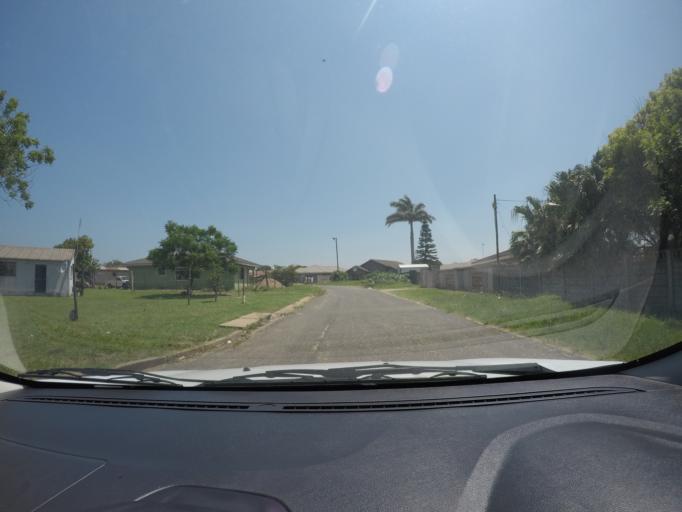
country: ZA
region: KwaZulu-Natal
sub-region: uThungulu District Municipality
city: eSikhawini
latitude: -28.8708
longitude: 31.9019
